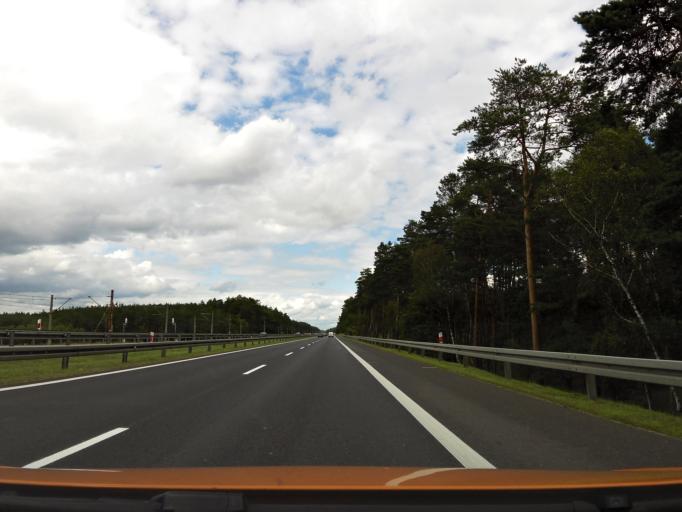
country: PL
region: West Pomeranian Voivodeship
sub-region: Powiat goleniowski
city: Goleniow
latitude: 53.5088
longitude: 14.8020
